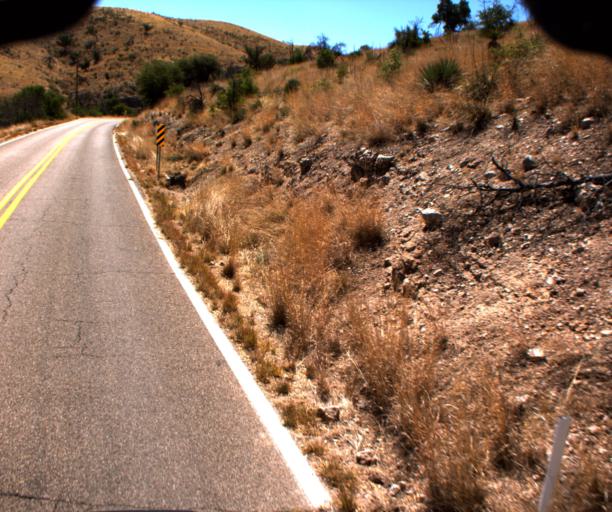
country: US
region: Arizona
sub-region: Santa Cruz County
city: Rio Rico
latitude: 31.3944
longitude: -111.0775
